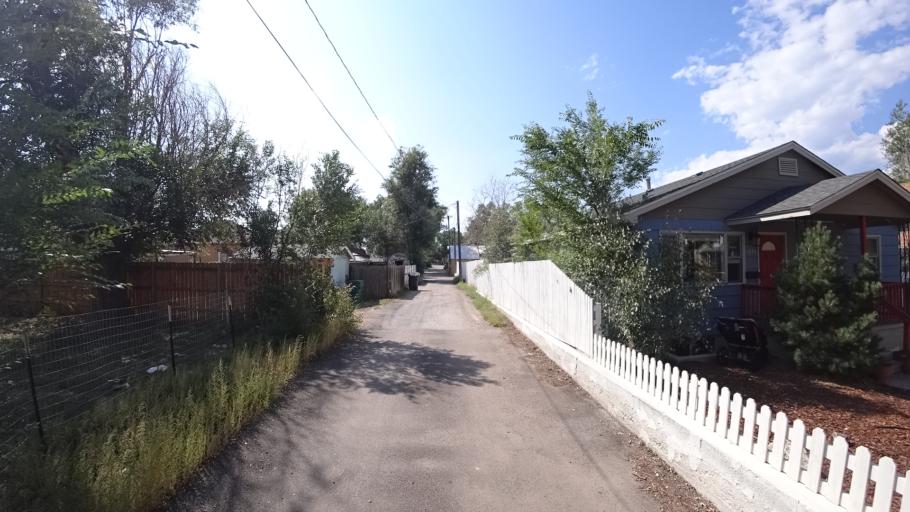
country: US
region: Colorado
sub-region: El Paso County
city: Colorado Springs
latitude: 38.8261
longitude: -104.8047
